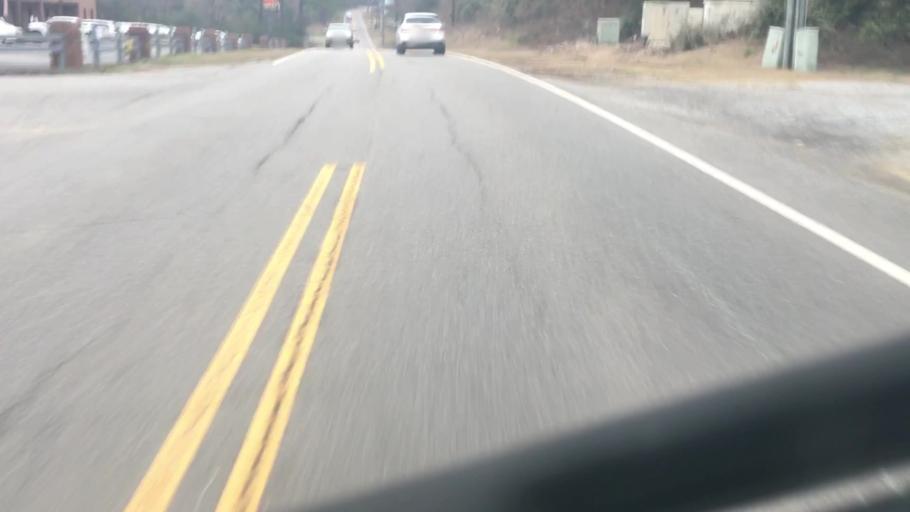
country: US
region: Alabama
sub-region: Jefferson County
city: Hoover
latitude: 33.3667
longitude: -86.8120
